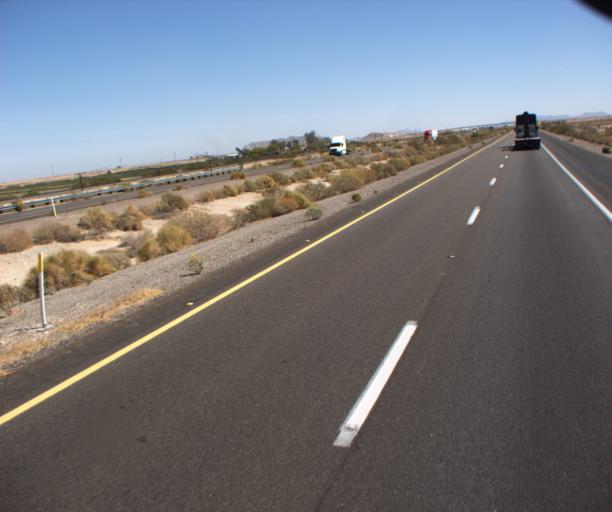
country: US
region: Arizona
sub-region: Yuma County
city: Wellton
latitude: 32.6729
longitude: -114.0895
